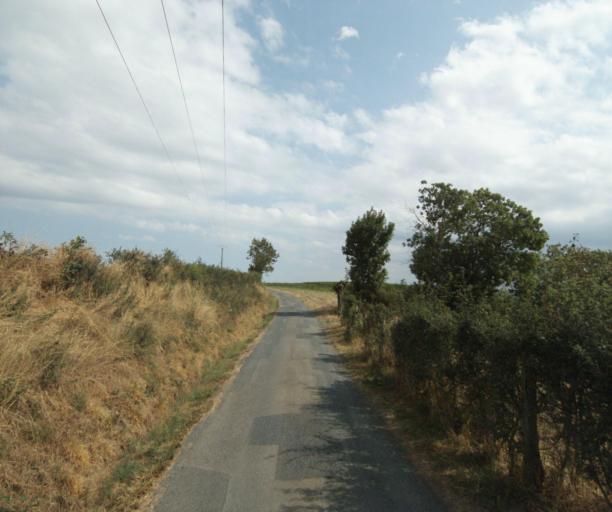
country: FR
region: Rhone-Alpes
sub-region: Departement du Rhone
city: Bully
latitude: 45.8513
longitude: 4.5734
